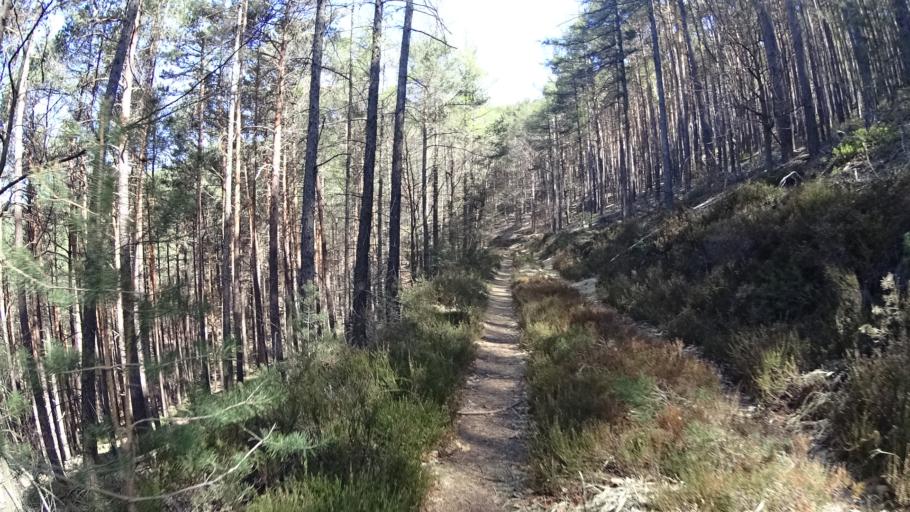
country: DE
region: Rheinland-Pfalz
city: Lambrecht
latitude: 49.3895
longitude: 8.0749
